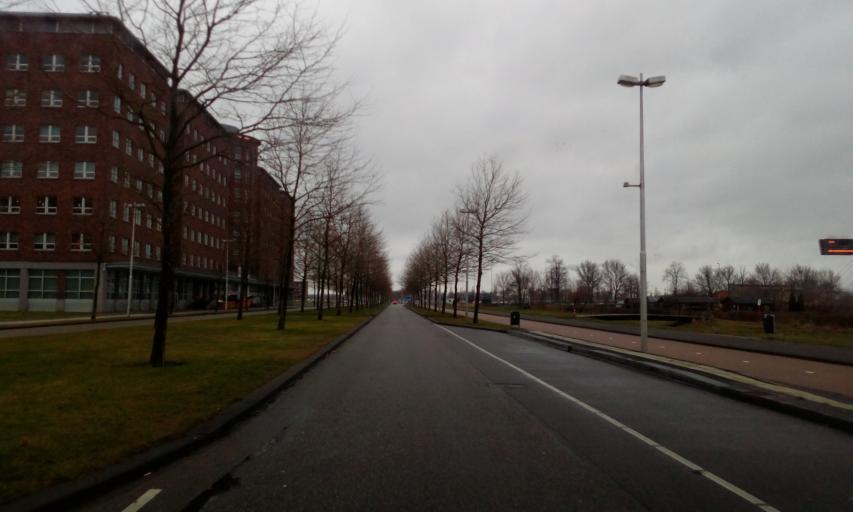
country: NL
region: Utrecht
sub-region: Gemeente Nieuwegein
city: Nieuwegein
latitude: 52.0663
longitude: 5.0859
